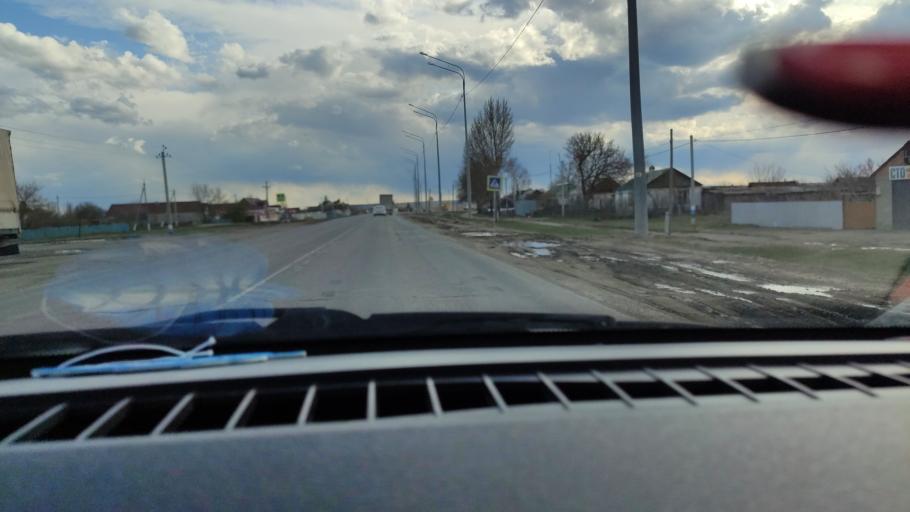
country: RU
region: Saratov
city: Sinodskoye
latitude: 51.9827
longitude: 46.6597
